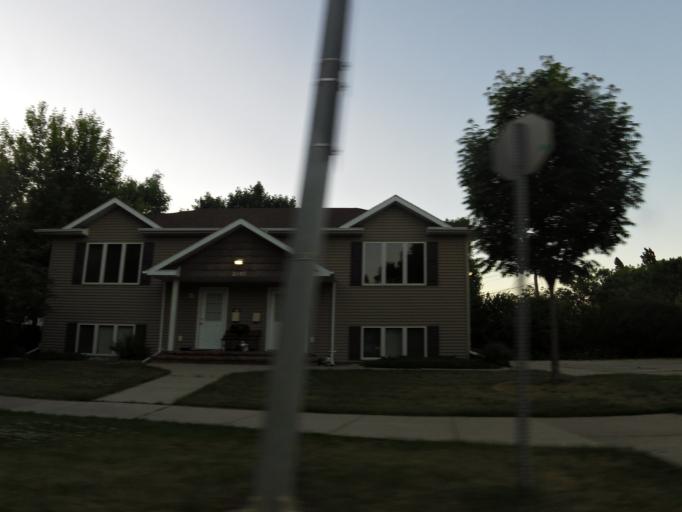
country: US
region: North Dakota
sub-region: Grand Forks County
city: Grand Forks
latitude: 47.9258
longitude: -97.0780
